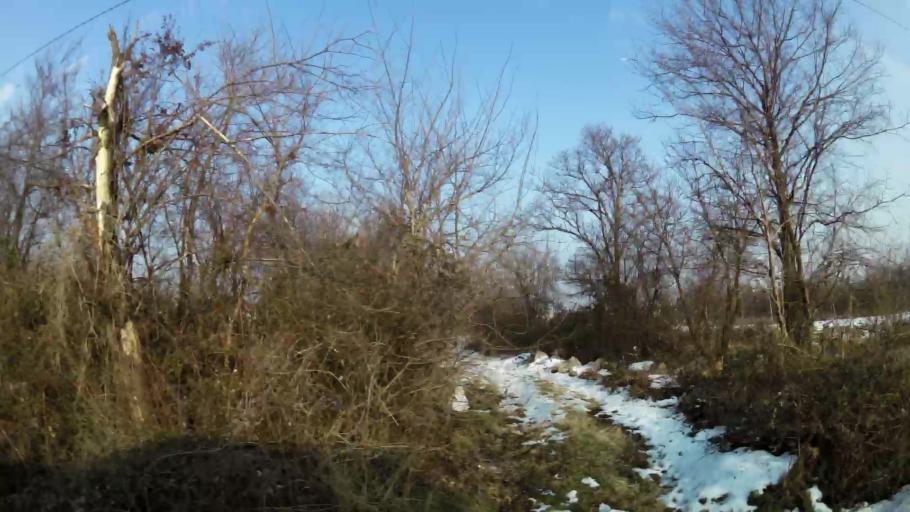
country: MK
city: Kadino
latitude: 41.9652
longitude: 21.5936
